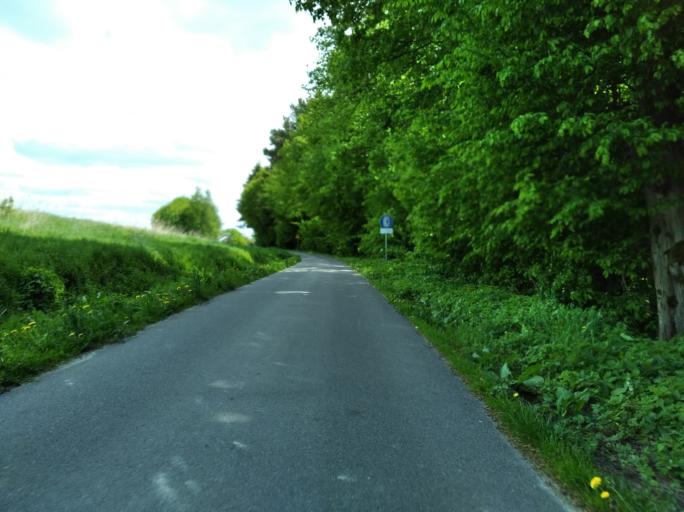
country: PL
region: Subcarpathian Voivodeship
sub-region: Powiat strzyzowski
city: Wisniowa
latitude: 49.8863
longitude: 21.6312
